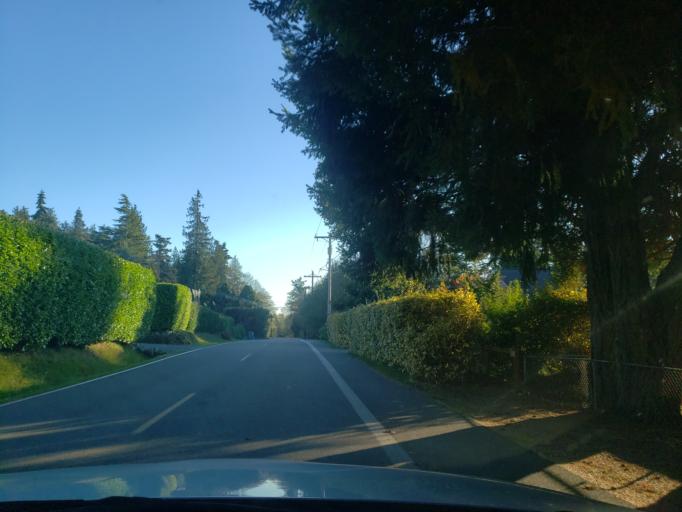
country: US
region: Washington
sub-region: Snohomish County
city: Woodway
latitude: 47.7832
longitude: -122.3856
